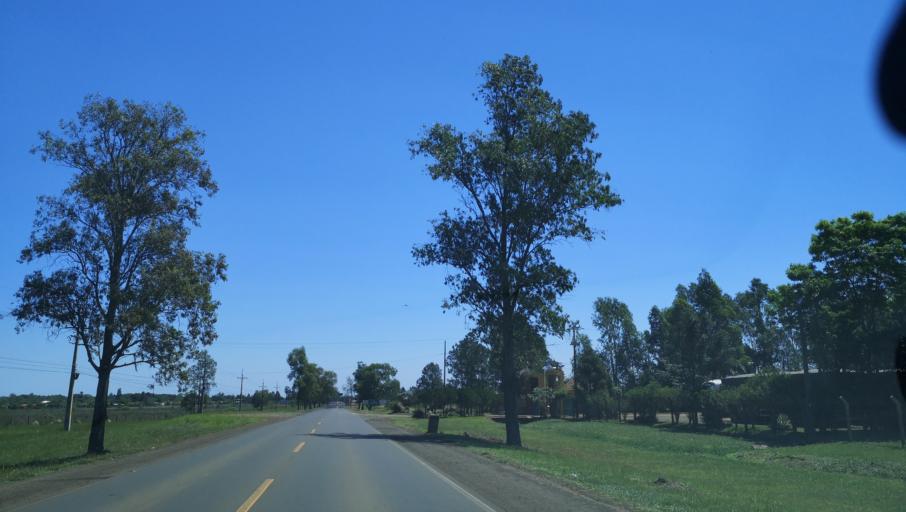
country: PY
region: Itapua
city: Carmen del Parana
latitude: -27.2206
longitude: -56.1299
